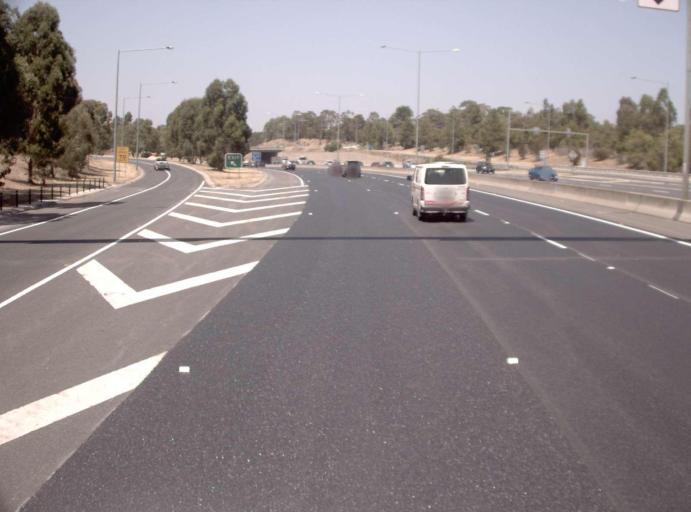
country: AU
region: Victoria
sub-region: Boroondara
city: Balwyn North
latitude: -37.7858
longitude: 145.1006
